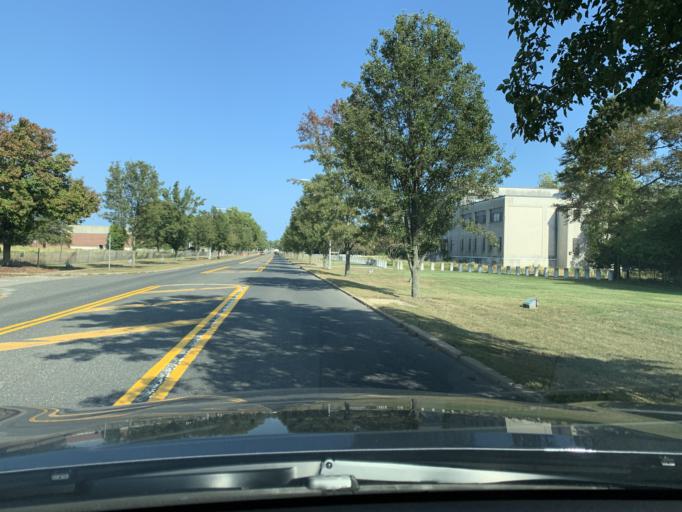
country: US
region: New Jersey
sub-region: Monmouth County
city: Eatontown
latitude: 40.3096
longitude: -74.0561
